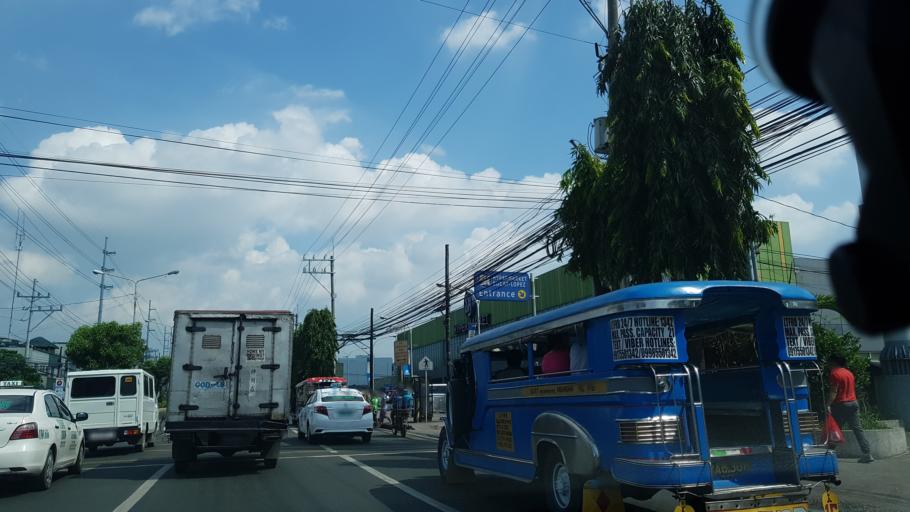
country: PH
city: Sambayanihan People's Village
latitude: 14.4696
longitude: 121.0102
